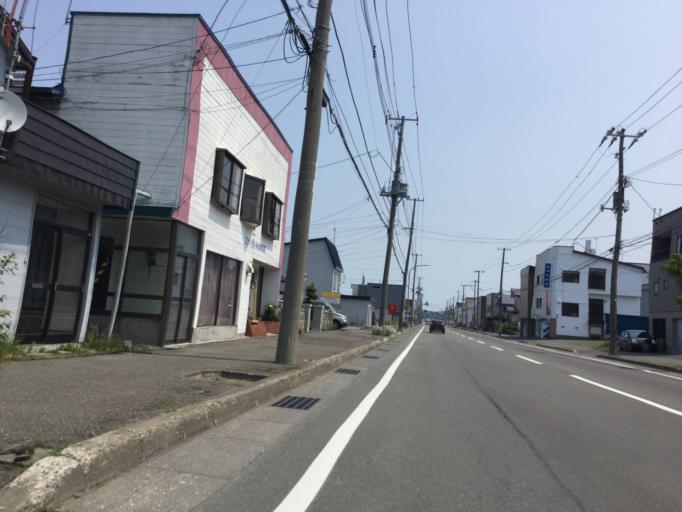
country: JP
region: Hokkaido
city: Wakkanai
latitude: 45.3950
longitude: 141.7016
